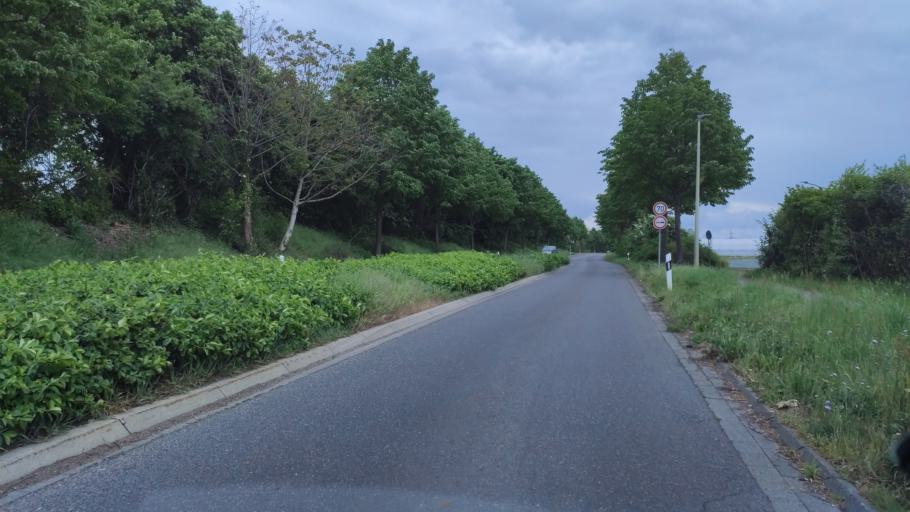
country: DE
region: North Rhine-Westphalia
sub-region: Regierungsbezirk Dusseldorf
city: Kaarst
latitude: 51.2109
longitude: 6.6225
